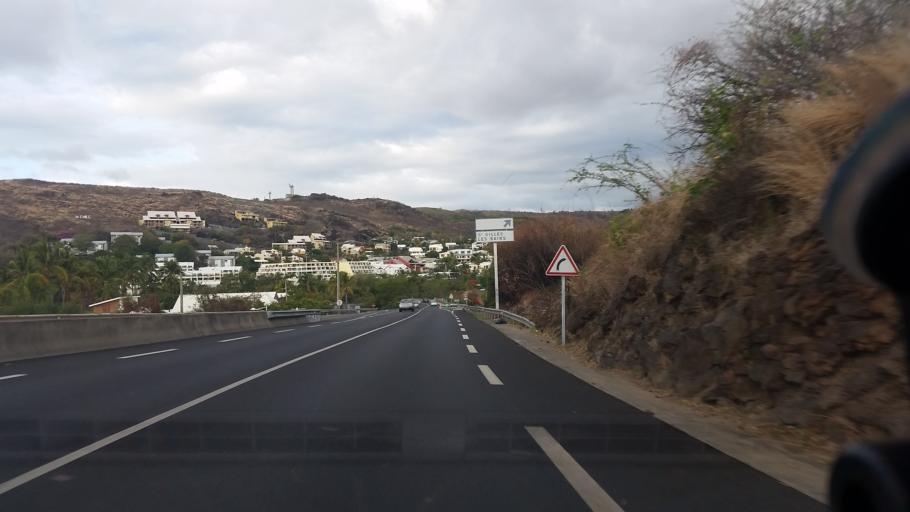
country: RE
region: Reunion
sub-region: Reunion
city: Saint-Paul
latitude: -21.0551
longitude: 55.2275
